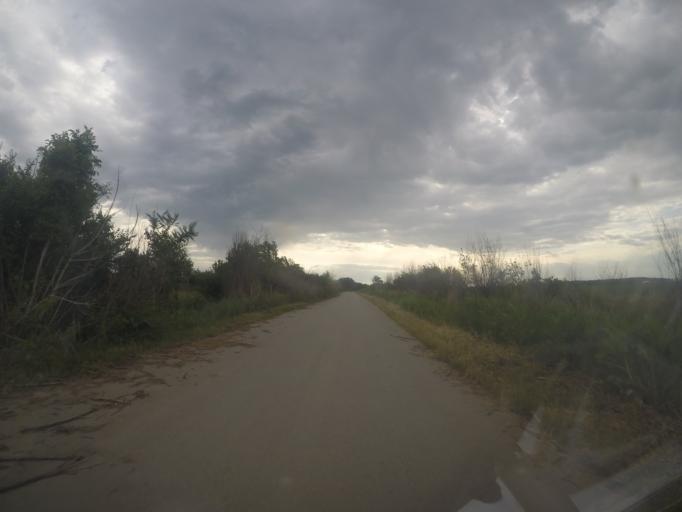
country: RS
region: Central Serbia
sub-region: Belgrade
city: Zemun
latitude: 44.8952
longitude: 20.3948
